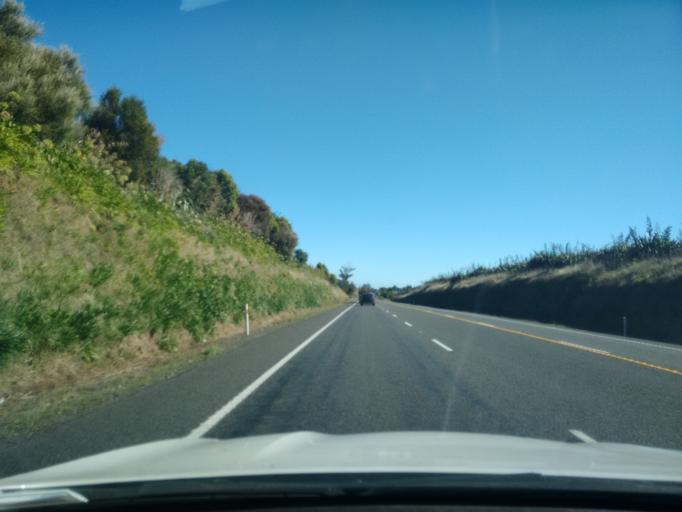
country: NZ
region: Taranaki
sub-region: New Plymouth District
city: New Plymouth
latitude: -39.1394
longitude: 174.1342
